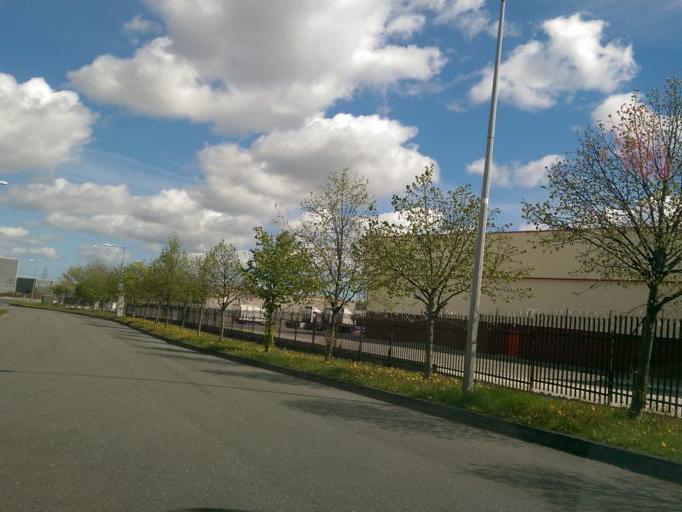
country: IE
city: Cherry Orchard
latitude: 53.3234
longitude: -6.3622
